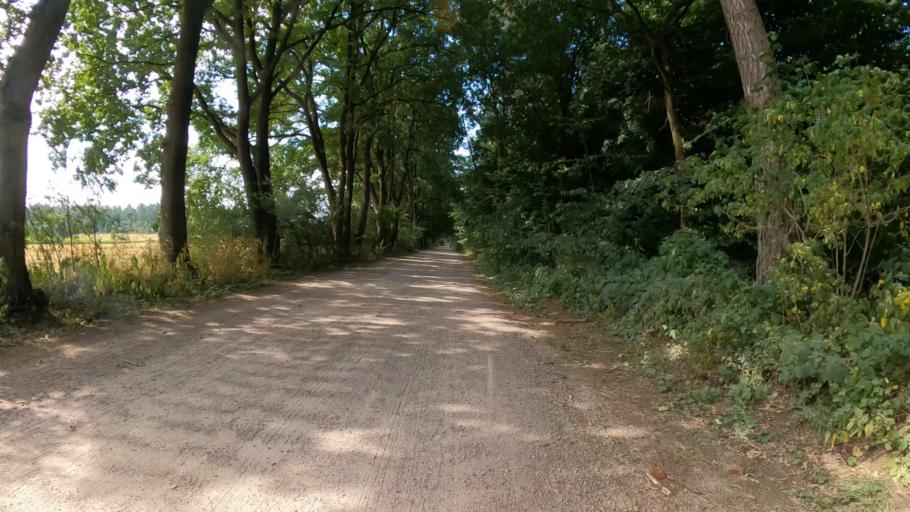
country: DE
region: Schleswig-Holstein
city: Hamwarde
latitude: 53.4288
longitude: 10.4199
